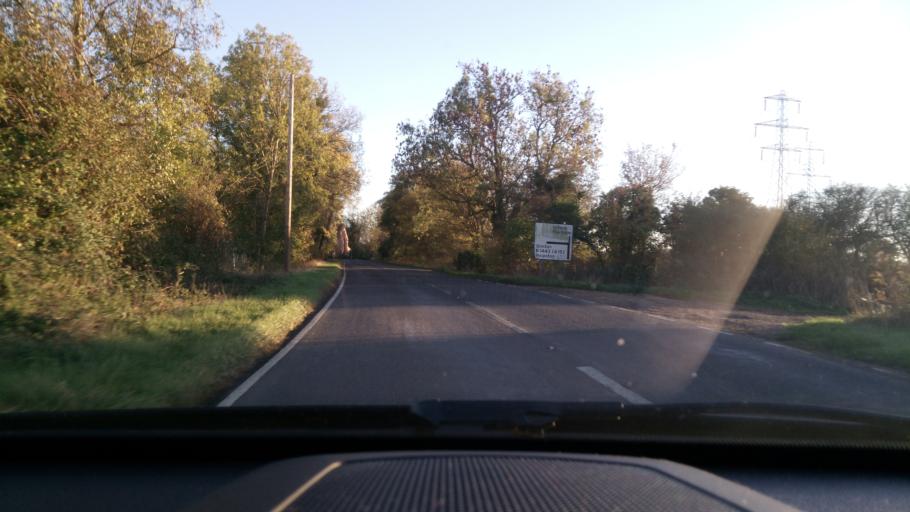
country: GB
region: England
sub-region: Peterborough
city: Helpston
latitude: 52.6365
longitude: -0.3583
